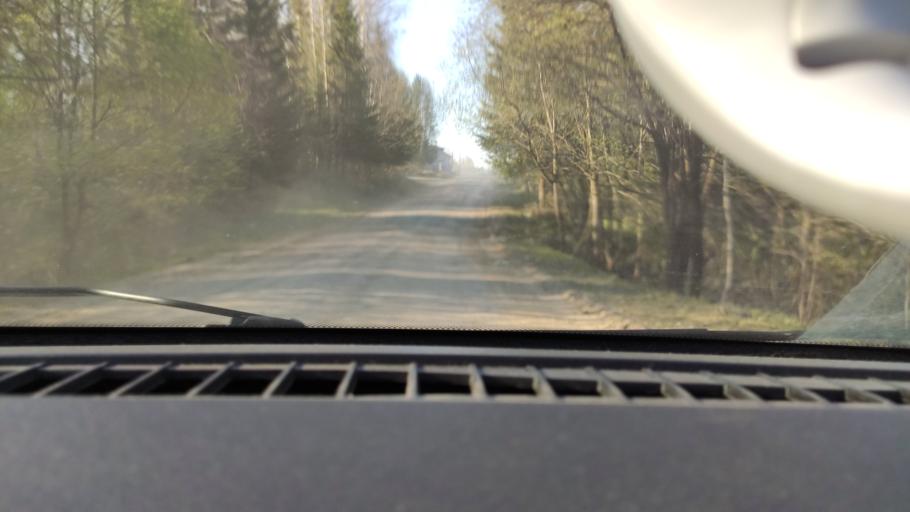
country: RU
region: Perm
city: Polazna
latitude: 58.1340
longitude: 56.4576
